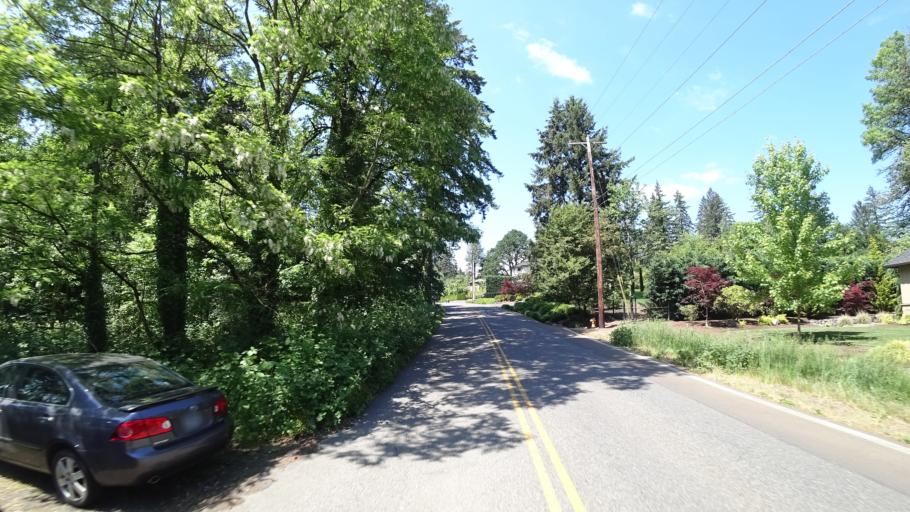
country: US
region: Oregon
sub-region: Clackamas County
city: Lake Oswego
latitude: 45.4254
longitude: -122.6961
